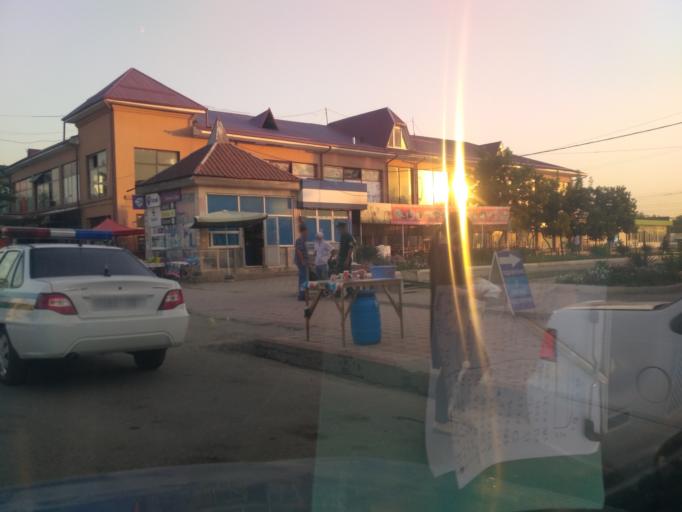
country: UZ
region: Sirdaryo
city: Guliston
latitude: 40.4940
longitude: 68.7667
